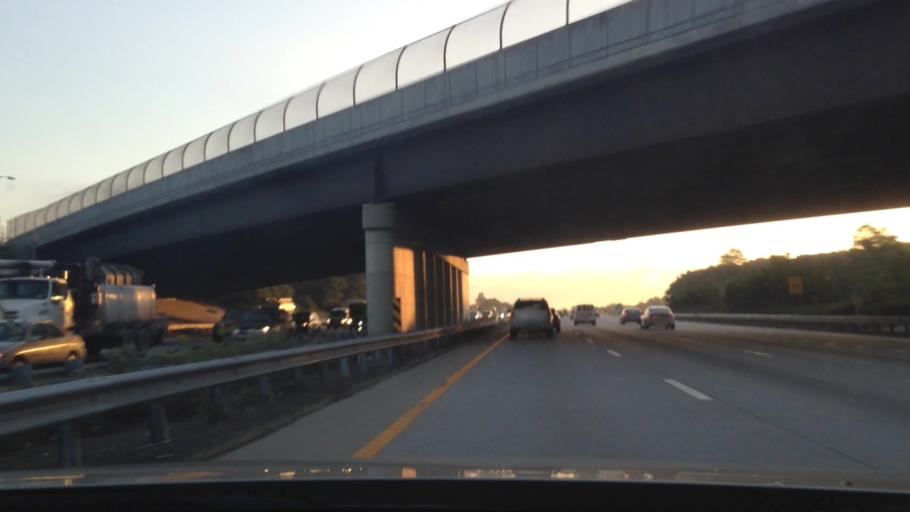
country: US
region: New York
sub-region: Suffolk County
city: Oakdale
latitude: 40.7520
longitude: -73.1251
